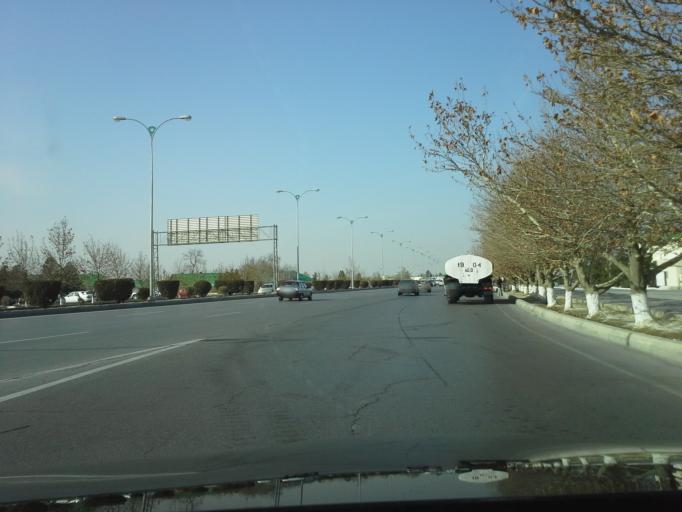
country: TM
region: Ahal
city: Abadan
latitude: 38.0522
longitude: 58.1844
